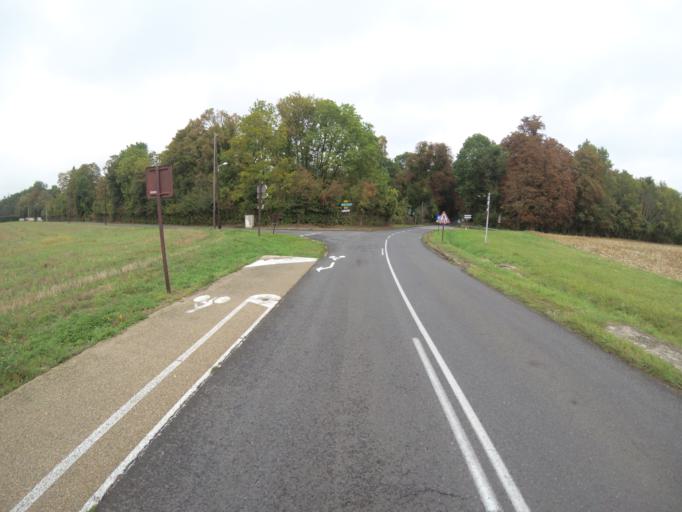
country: FR
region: Ile-de-France
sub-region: Departement de Seine-et-Marne
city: Guermantes
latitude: 48.8600
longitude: 2.7033
